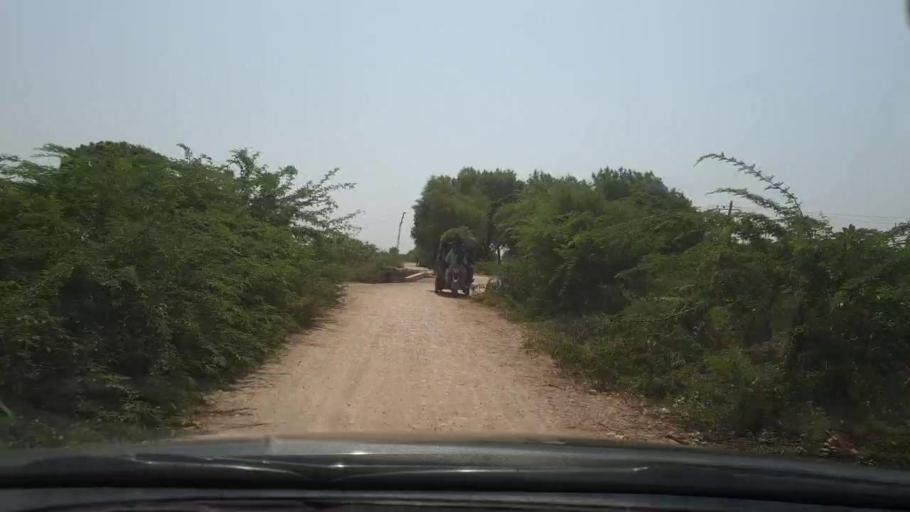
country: PK
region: Sindh
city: Tando Bago
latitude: 24.7821
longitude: 69.1823
